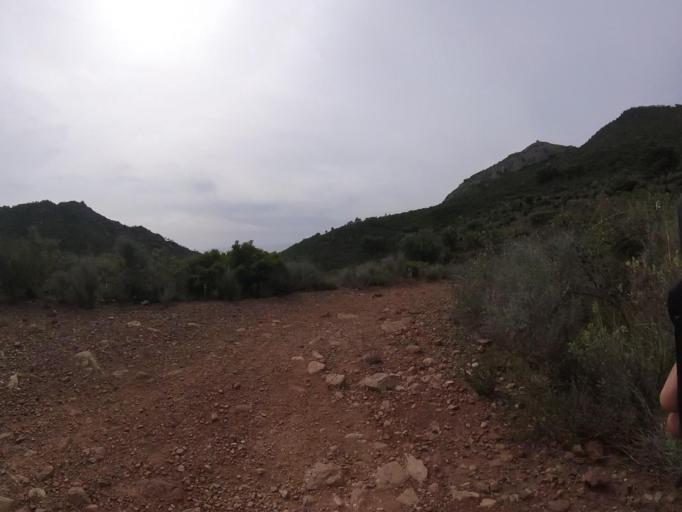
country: ES
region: Valencia
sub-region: Provincia de Castello
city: Benicassim
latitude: 40.0717
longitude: 0.0363
